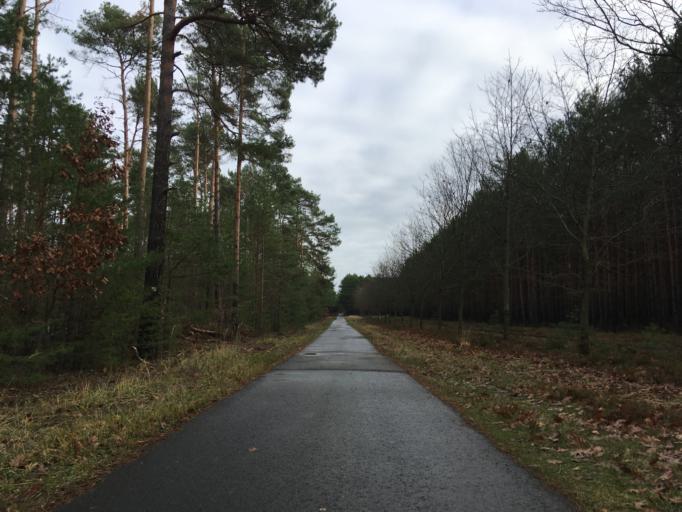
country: DE
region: Brandenburg
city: Tauer
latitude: 51.9190
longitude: 14.4813
